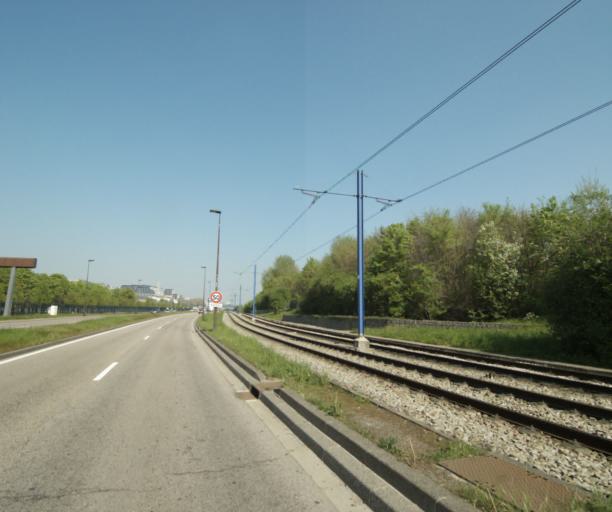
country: FR
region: Ile-de-France
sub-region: Departement des Hauts-de-Seine
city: Sevres
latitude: 48.8323
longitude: 2.2224
